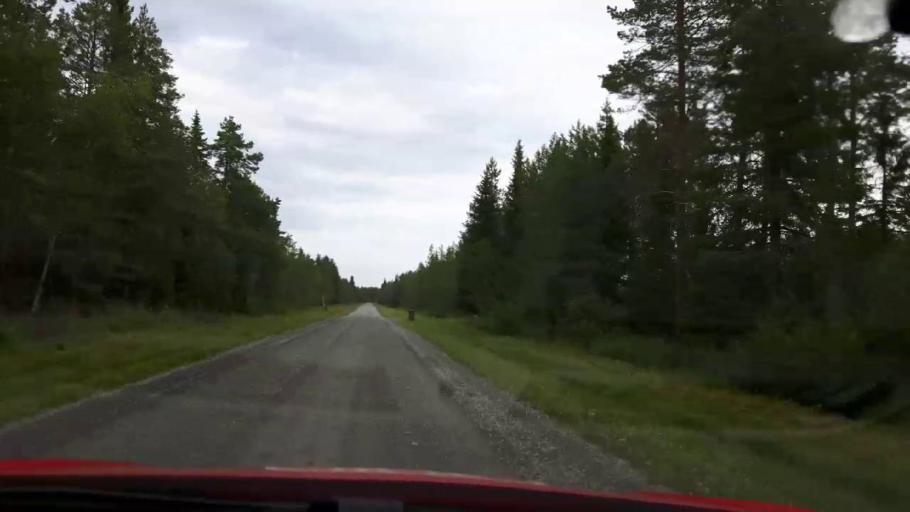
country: SE
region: Jaemtland
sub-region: Stroemsunds Kommun
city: Stroemsund
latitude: 63.7327
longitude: 15.5532
